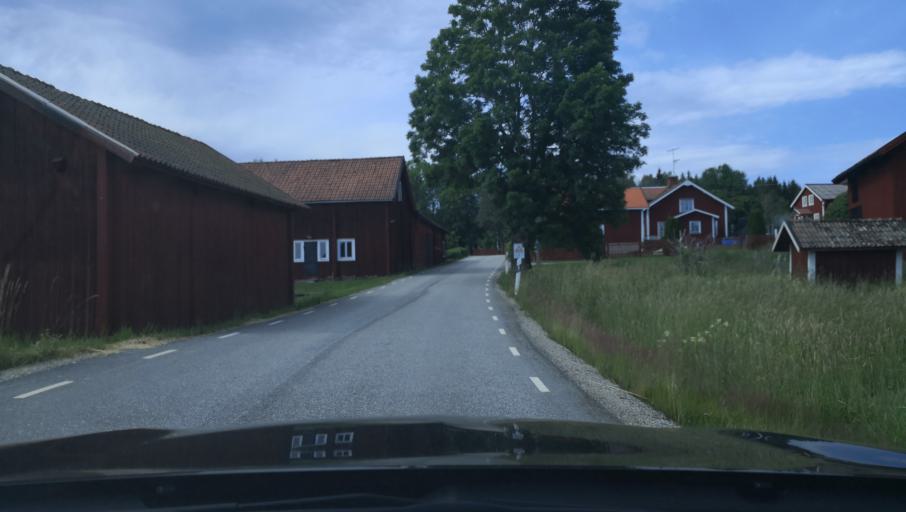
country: SE
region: Vaestmanland
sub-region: Norbergs Kommun
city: Norberg
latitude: 59.9801
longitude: 15.9585
